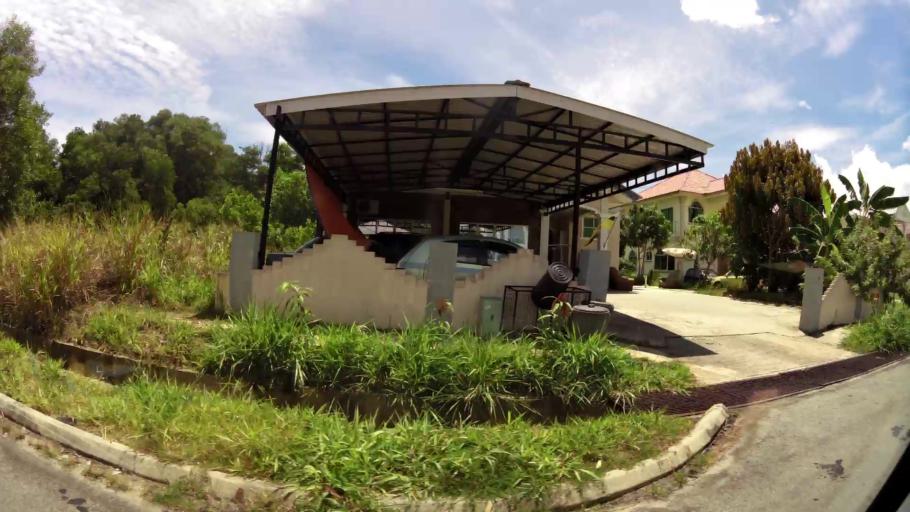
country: BN
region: Brunei and Muara
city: Bandar Seri Begawan
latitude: 4.9688
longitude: 114.9024
